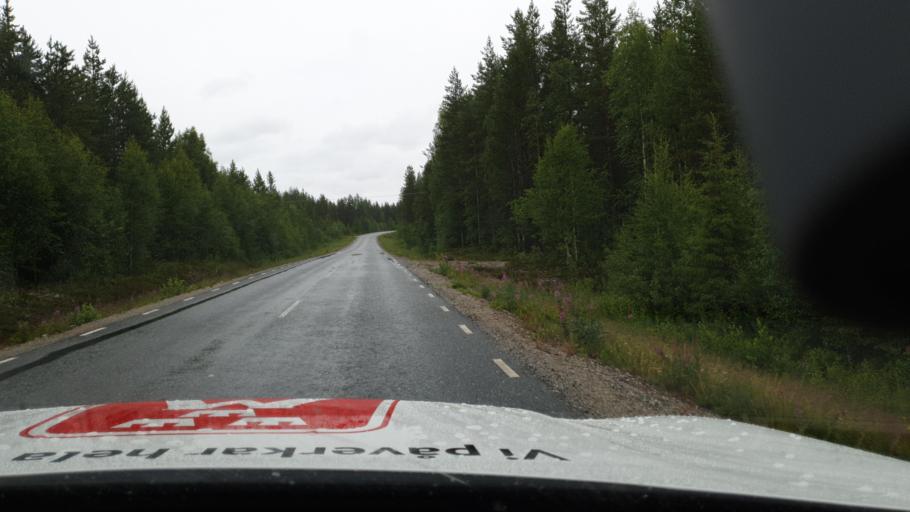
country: SE
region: Vaesterbotten
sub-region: Vindelns Kommun
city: Vindeln
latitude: 64.4273
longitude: 19.7024
